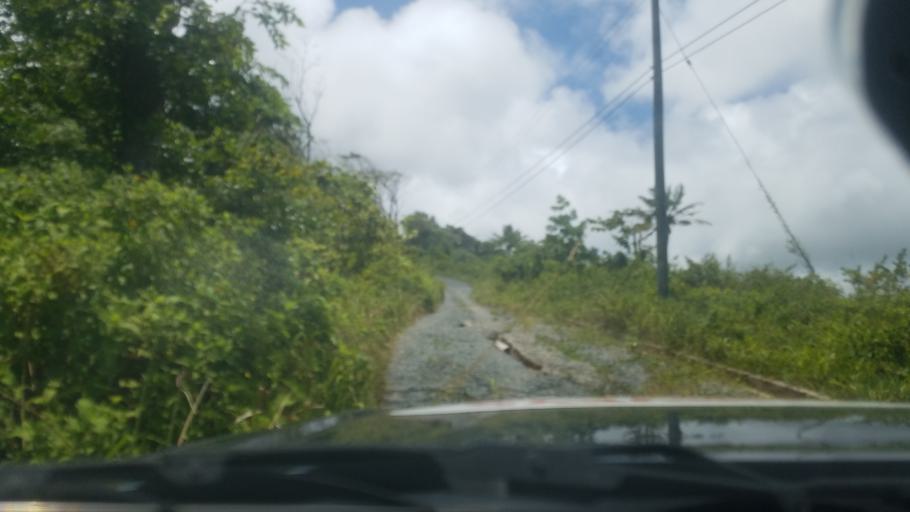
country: LC
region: Praslin
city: Praslin
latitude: 13.8724
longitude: -60.9140
